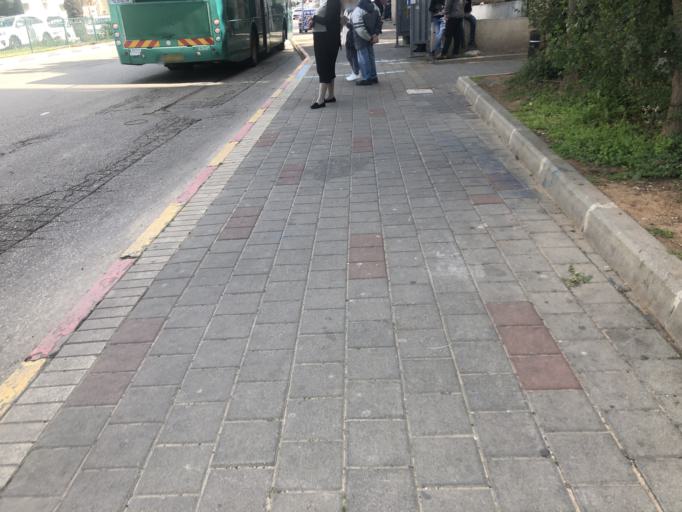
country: IL
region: Haifa
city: Hadera
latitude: 32.4399
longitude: 34.9189
